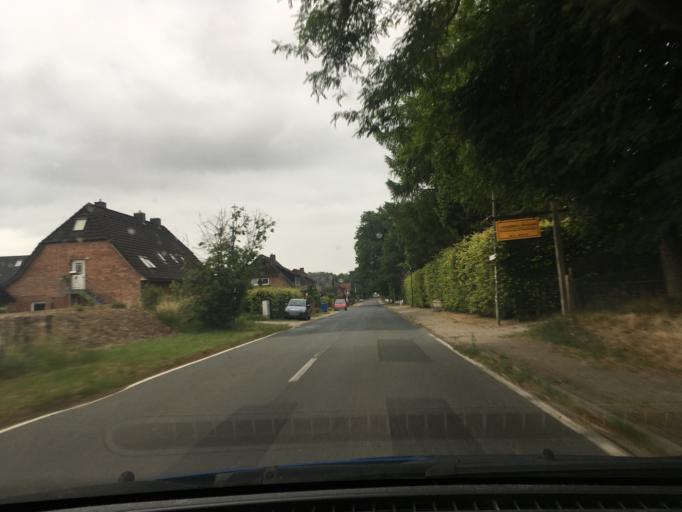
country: DE
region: Lower Saxony
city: Egestorf
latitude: 53.1982
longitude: 10.0651
